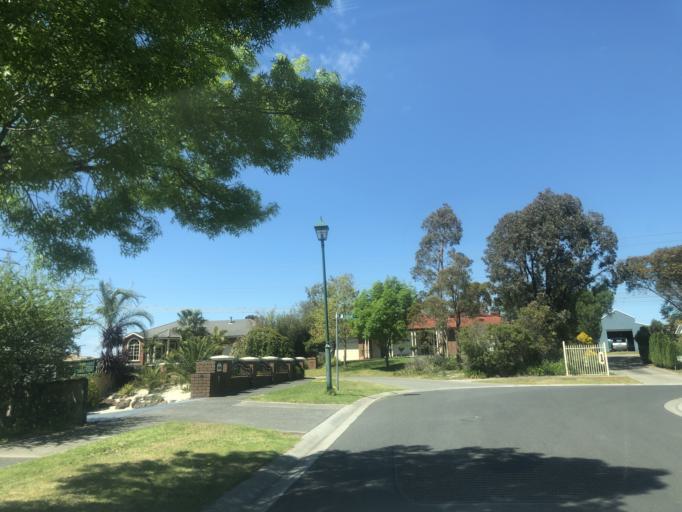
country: AU
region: Victoria
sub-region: Casey
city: Narre Warren North
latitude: -37.9911
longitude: 145.2865
